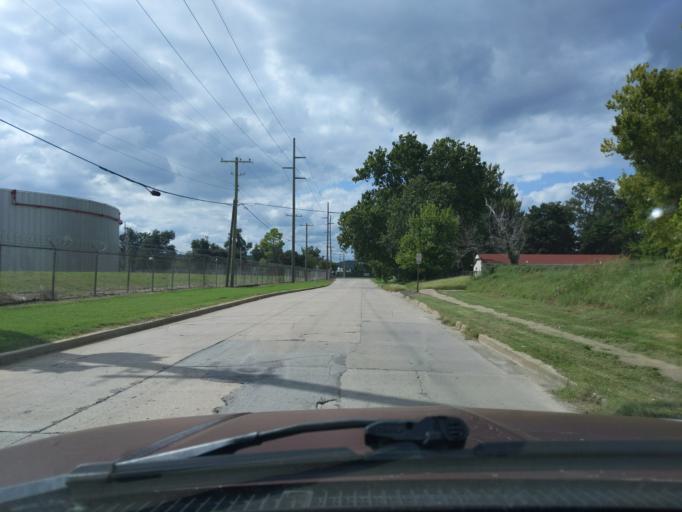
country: US
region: Oklahoma
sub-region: Tulsa County
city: Tulsa
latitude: 36.1263
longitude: -96.0047
